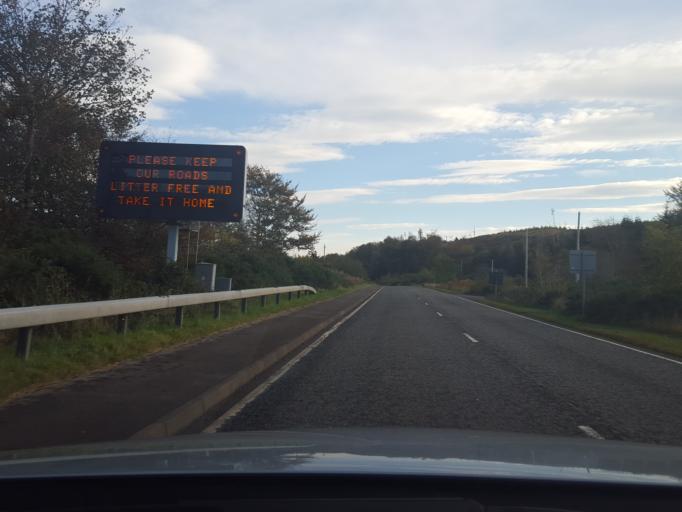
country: GB
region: Scotland
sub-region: Highland
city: Portree
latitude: 57.2822
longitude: -5.6214
